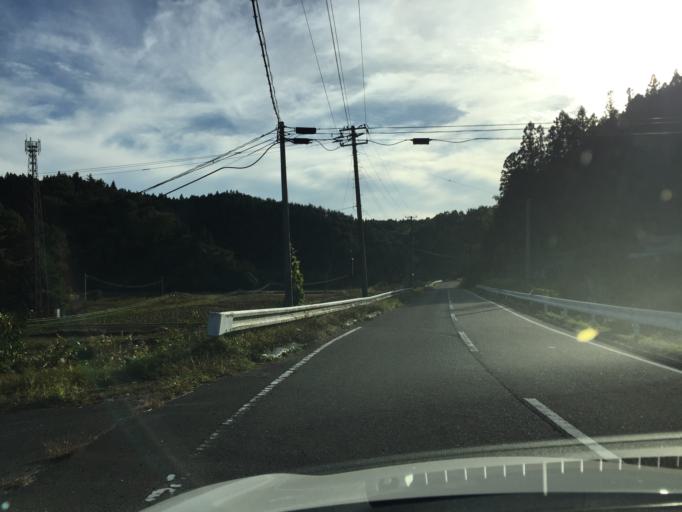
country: JP
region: Fukushima
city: Ishikawa
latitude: 37.2070
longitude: 140.5962
